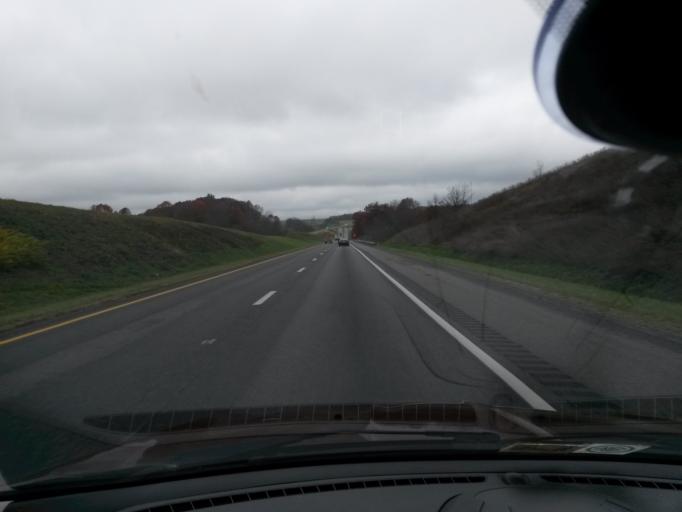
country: US
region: Virginia
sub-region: Pulaski County
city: Pulaski
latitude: 36.9247
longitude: -80.9040
